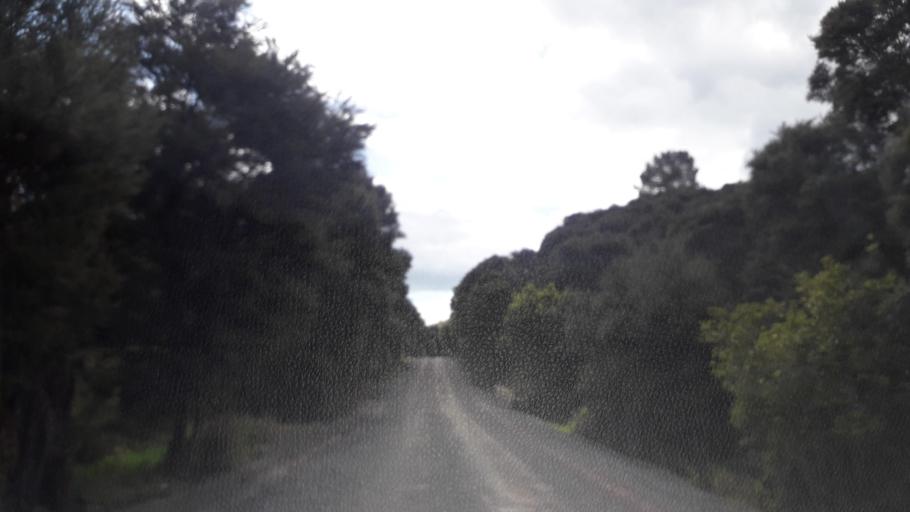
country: NZ
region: Northland
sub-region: Far North District
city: Paihia
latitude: -35.3013
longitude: 174.2206
